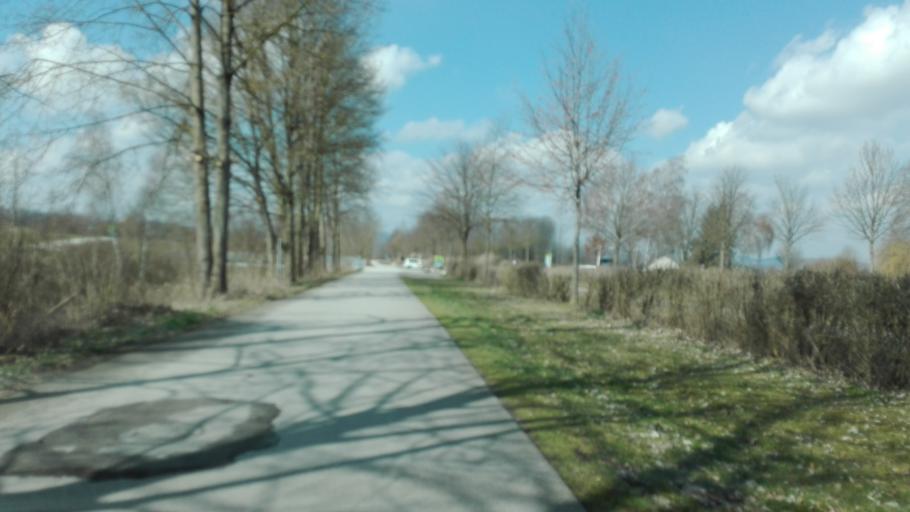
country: AT
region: Upper Austria
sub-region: Politischer Bezirk Urfahr-Umgebung
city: Feldkirchen an der Donau
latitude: 48.3206
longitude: 14.0703
